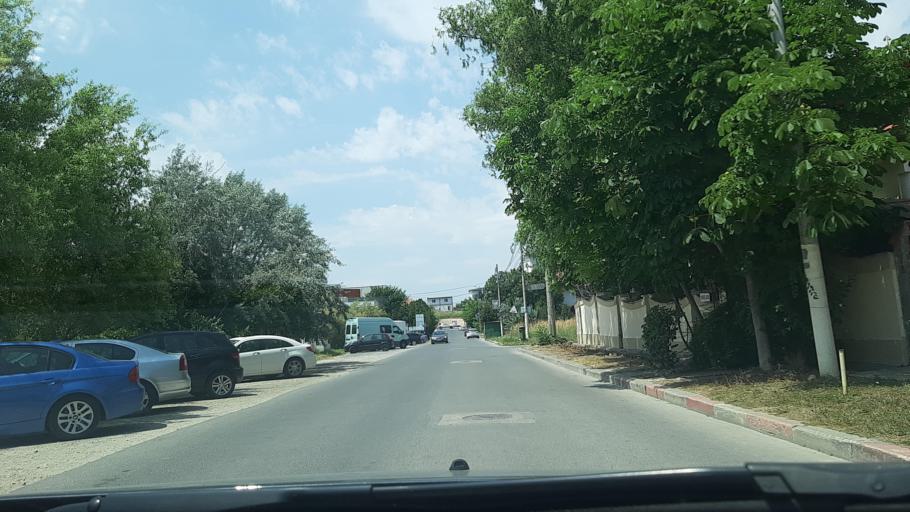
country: RO
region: Constanta
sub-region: Comuna Navodari
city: Navodari
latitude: 44.3002
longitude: 28.6222
